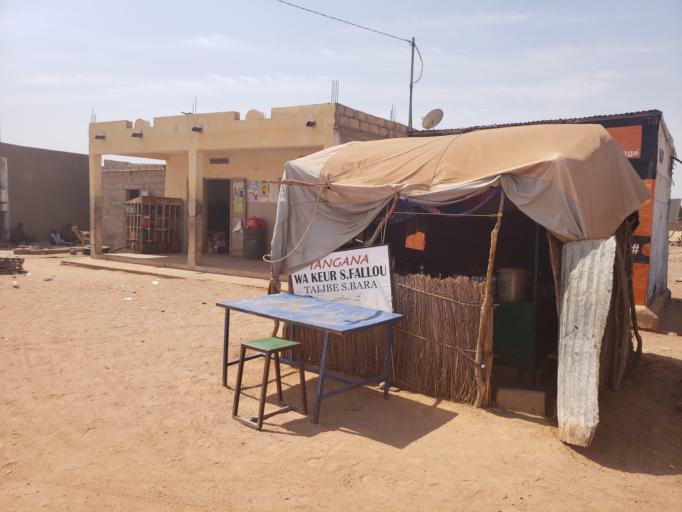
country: SN
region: Matam
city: Ranerou
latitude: 15.2980
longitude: -13.9571
